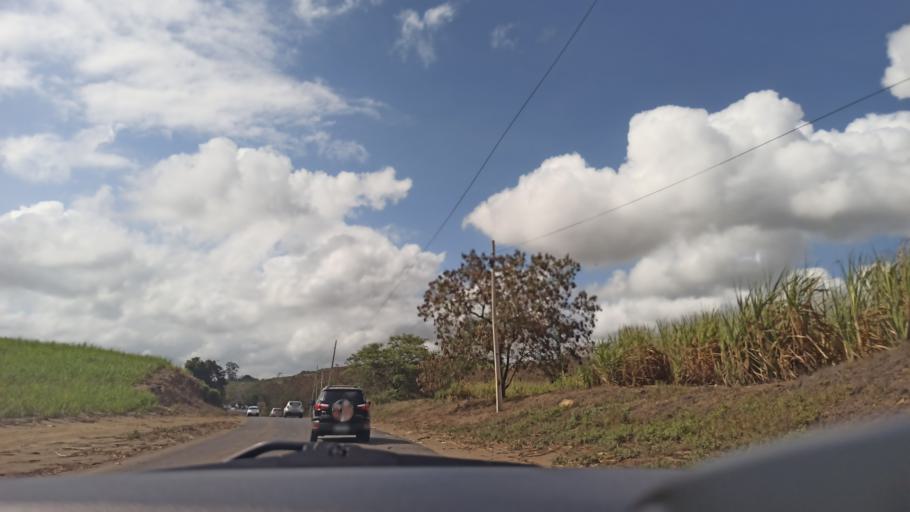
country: BR
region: Paraiba
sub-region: Juripiranga
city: Juripiranga
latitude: -7.4124
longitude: -35.2618
